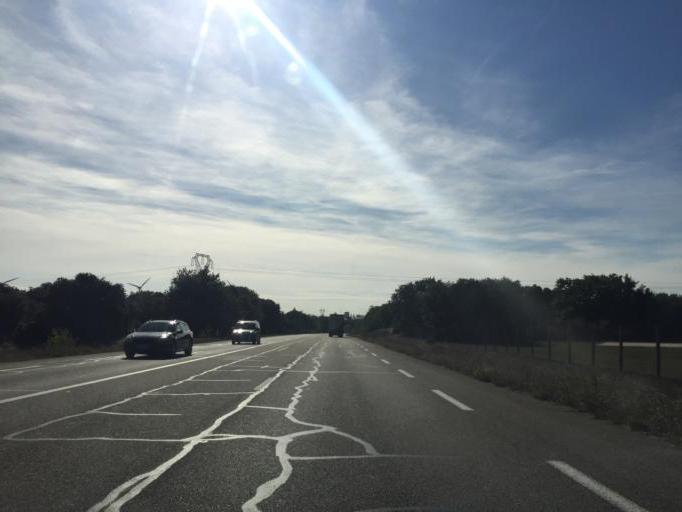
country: FR
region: Rhone-Alpes
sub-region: Departement de la Drome
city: Malataverne
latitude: 44.4562
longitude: 4.7527
